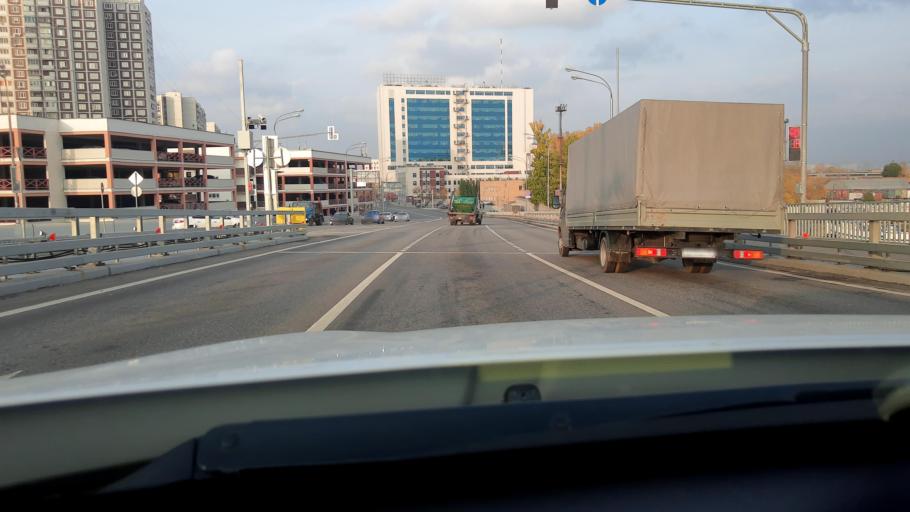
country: RU
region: Moskovskaya
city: Kozhukhovo
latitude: 55.6985
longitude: 37.6849
